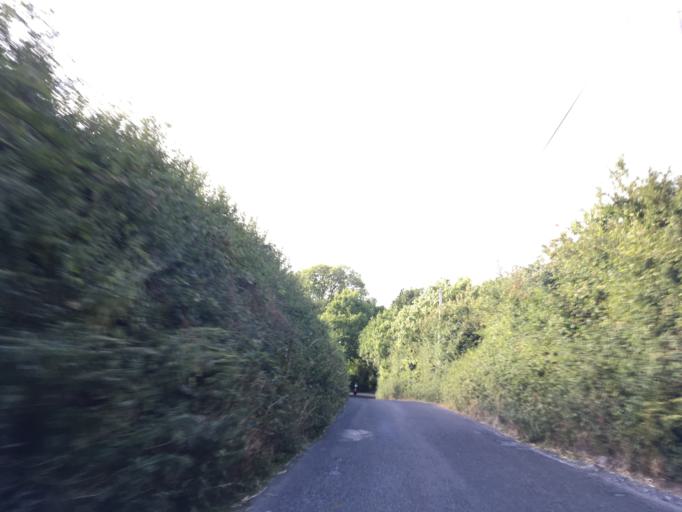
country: IE
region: Munster
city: Cahir
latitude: 52.2740
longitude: -7.9567
